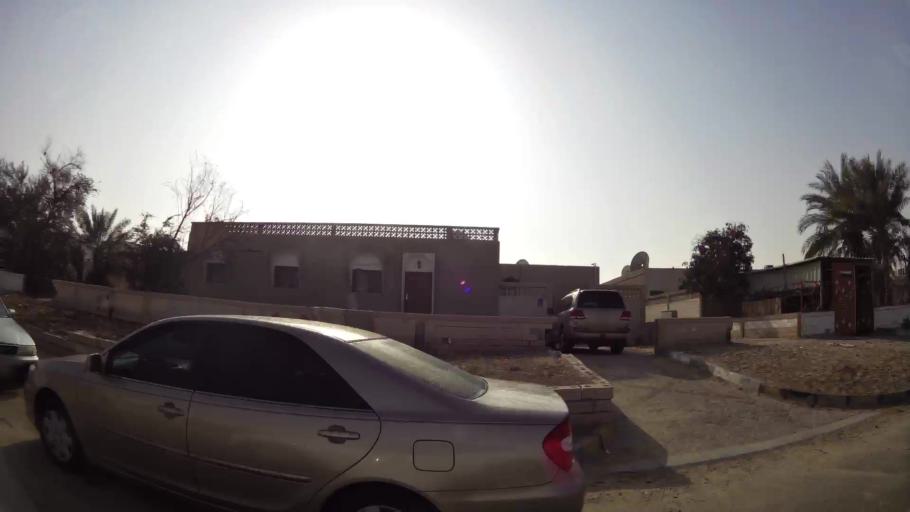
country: AE
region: Abu Dhabi
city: Abu Dhabi
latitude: 24.2704
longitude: 54.6447
